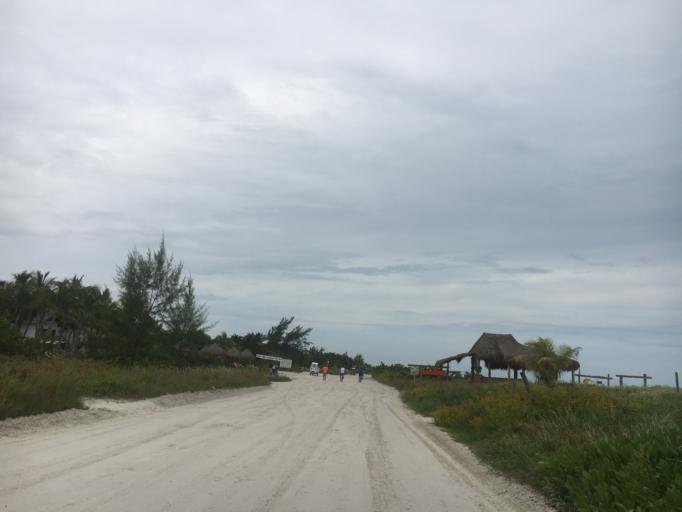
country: MX
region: Quintana Roo
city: Kantunilkin
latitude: 21.5287
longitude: -87.3732
